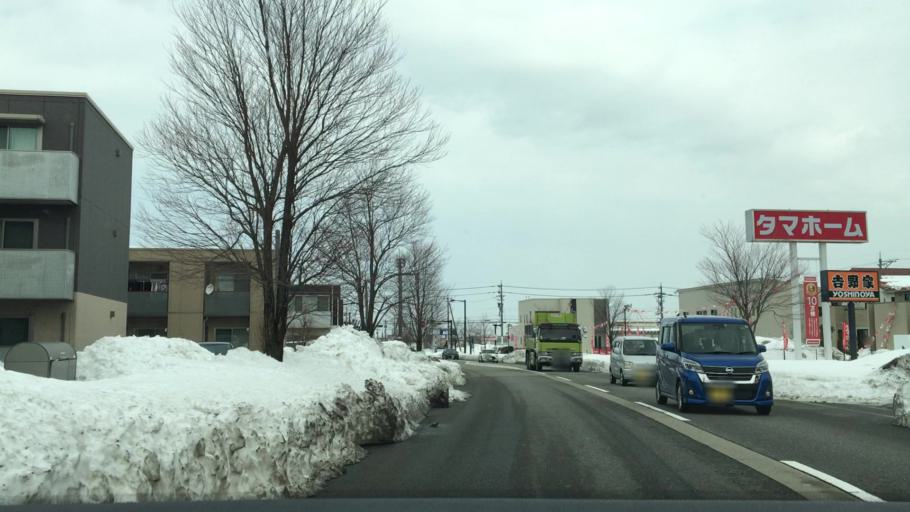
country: JP
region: Ishikawa
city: Nonoichi
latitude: 36.5103
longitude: 136.6086
